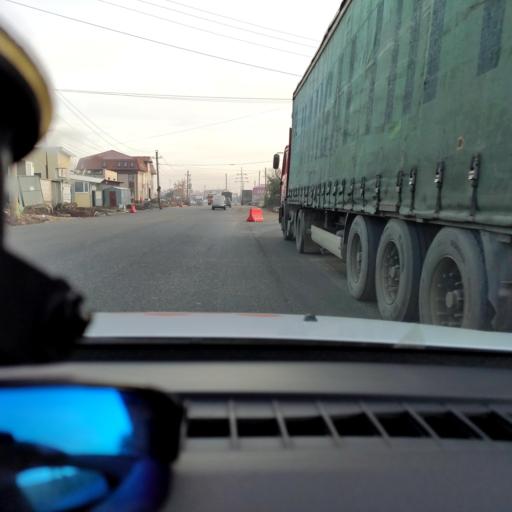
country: RU
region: Samara
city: Samara
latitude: 53.1833
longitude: 50.2159
